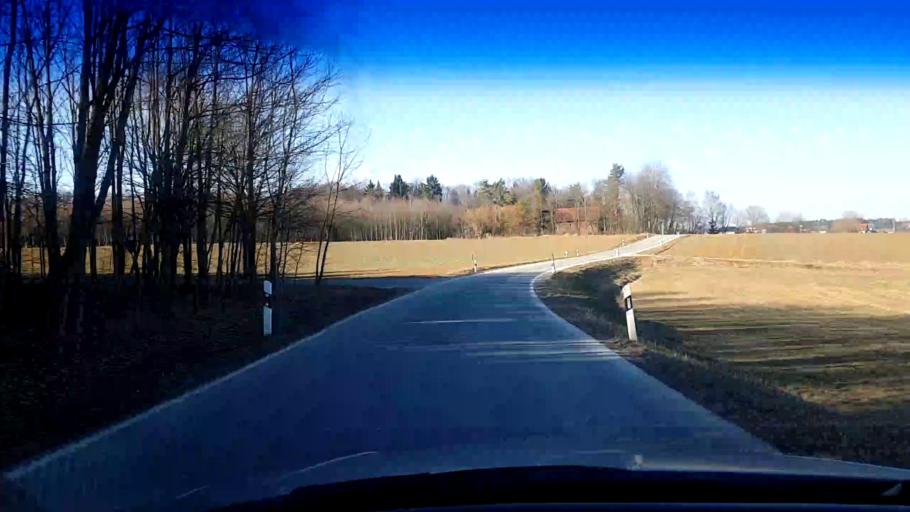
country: DE
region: Bavaria
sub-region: Upper Franconia
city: Aufsess
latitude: 49.9214
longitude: 11.2189
